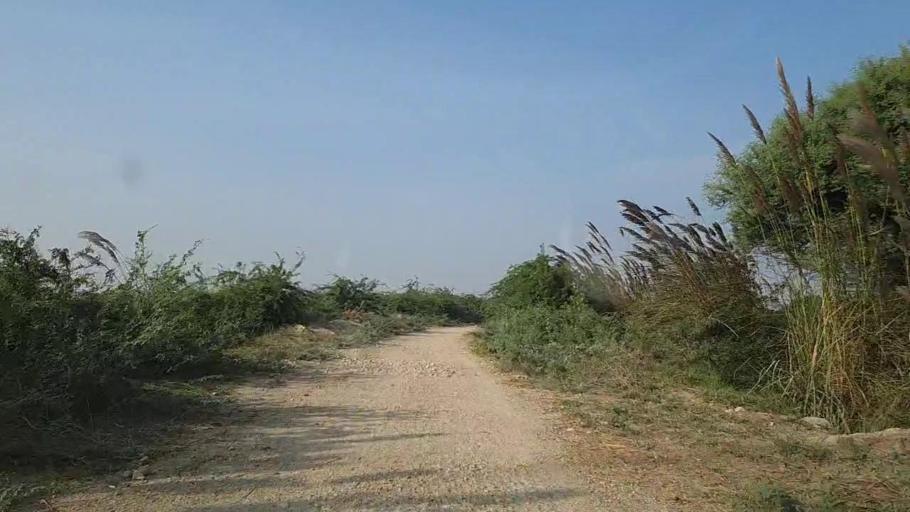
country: PK
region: Sindh
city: Mirpur Sakro
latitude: 24.5935
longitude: 67.6486
